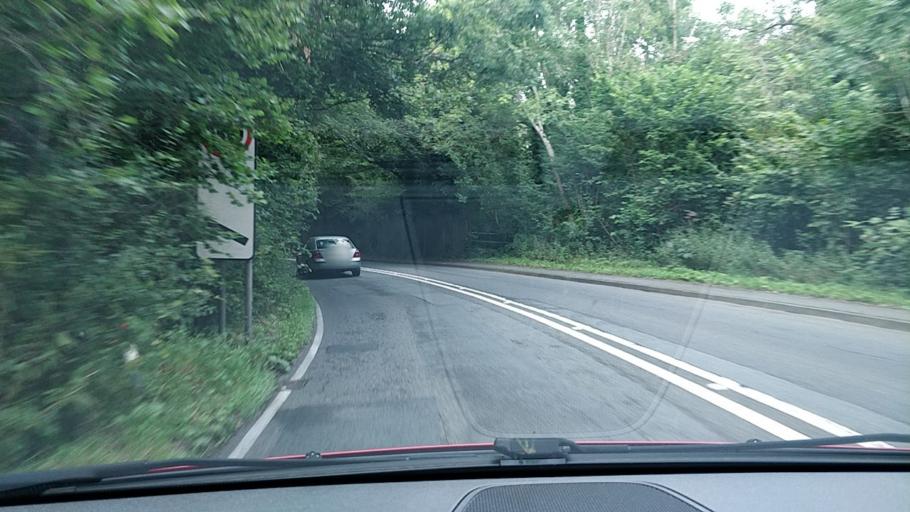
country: GB
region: Wales
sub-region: County of Flintshire
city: Leeswood
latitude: 53.1184
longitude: -3.0984
